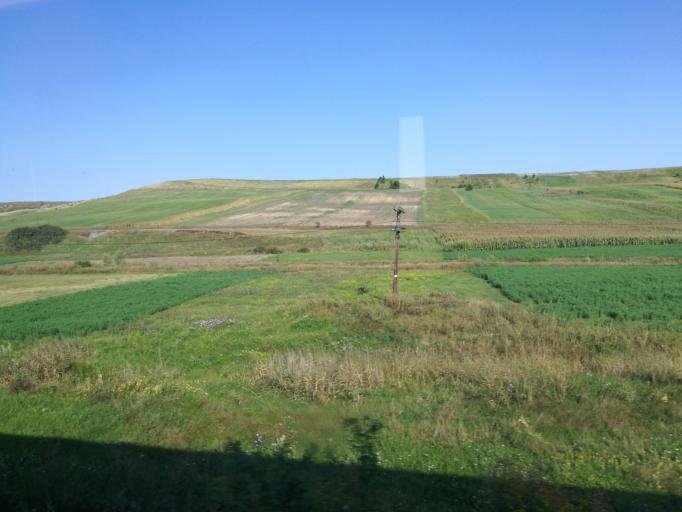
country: RO
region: Vaslui
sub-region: Comuna Rebricea
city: Rebricea
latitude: 46.8662
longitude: 27.5645
